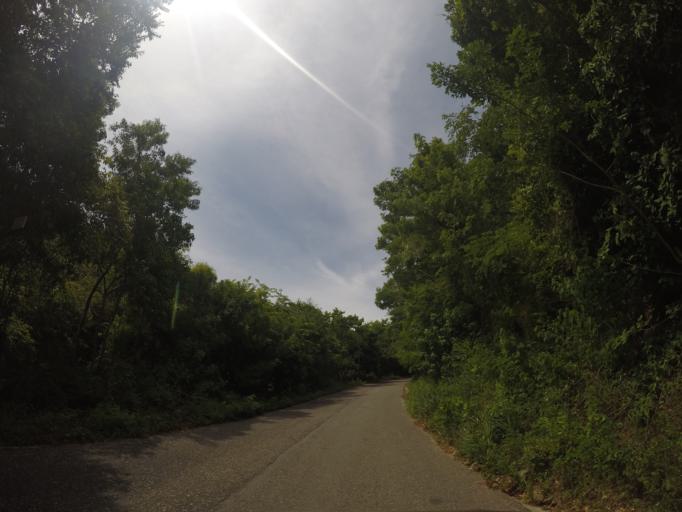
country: MX
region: Oaxaca
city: Santa Maria Tonameca
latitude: 15.6671
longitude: -96.5314
